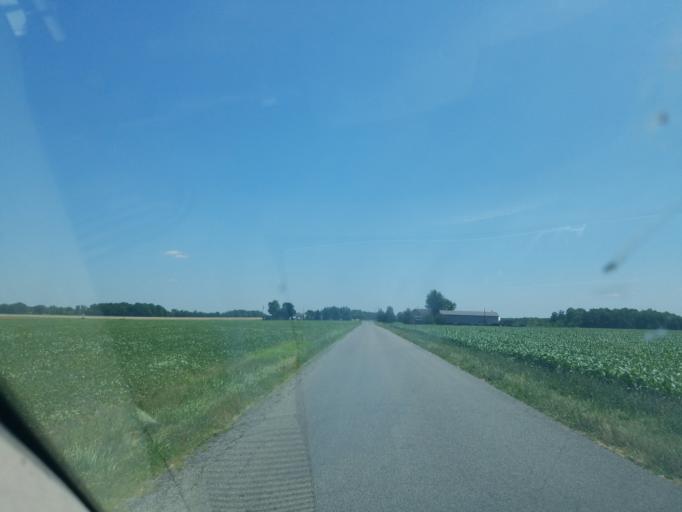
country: US
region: Ohio
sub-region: Allen County
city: Spencerville
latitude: 40.7576
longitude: -84.3530
